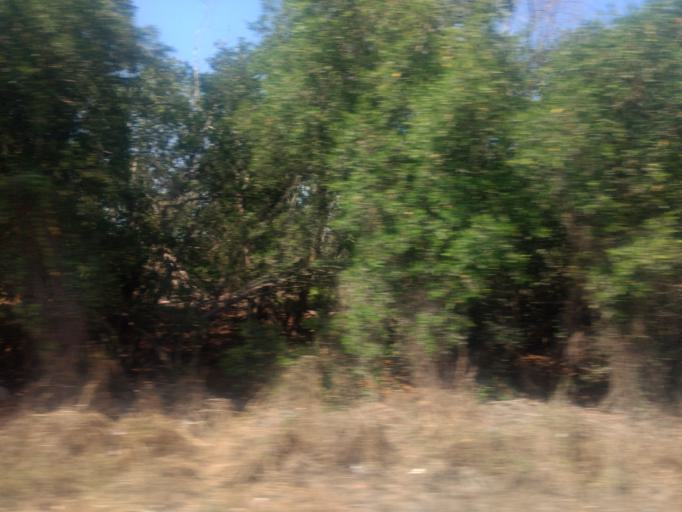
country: MX
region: Colima
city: El Colomo
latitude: 19.0487
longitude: -104.2645
